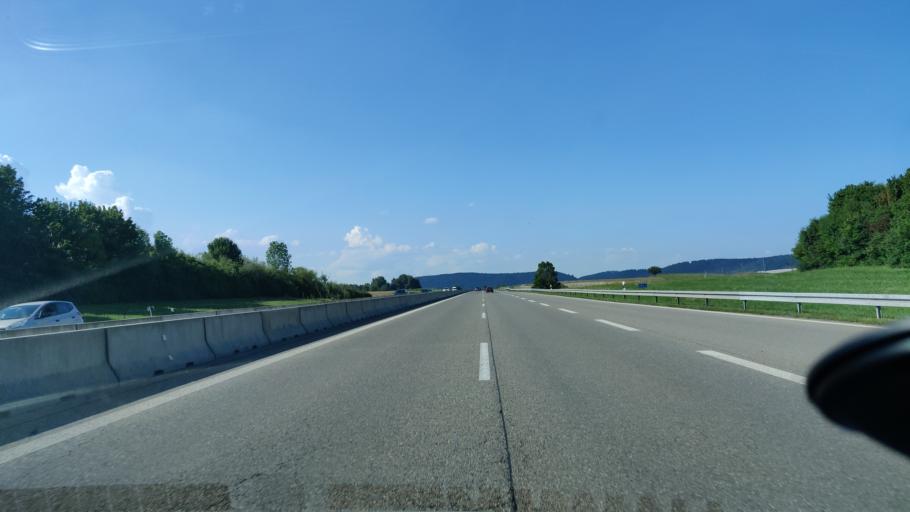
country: DE
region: Baden-Wuerttemberg
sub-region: Freiburg Region
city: Dietingen
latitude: 48.2445
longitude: 8.6473
